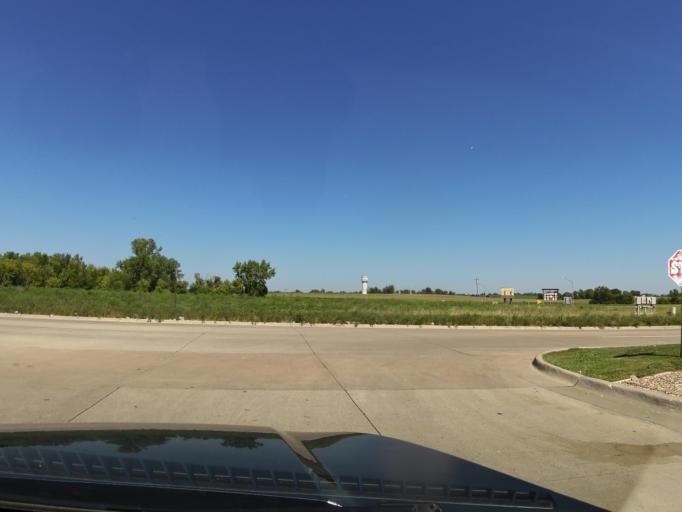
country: US
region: Iowa
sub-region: Linn County
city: Center Point
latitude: 42.1732
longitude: -91.7768
